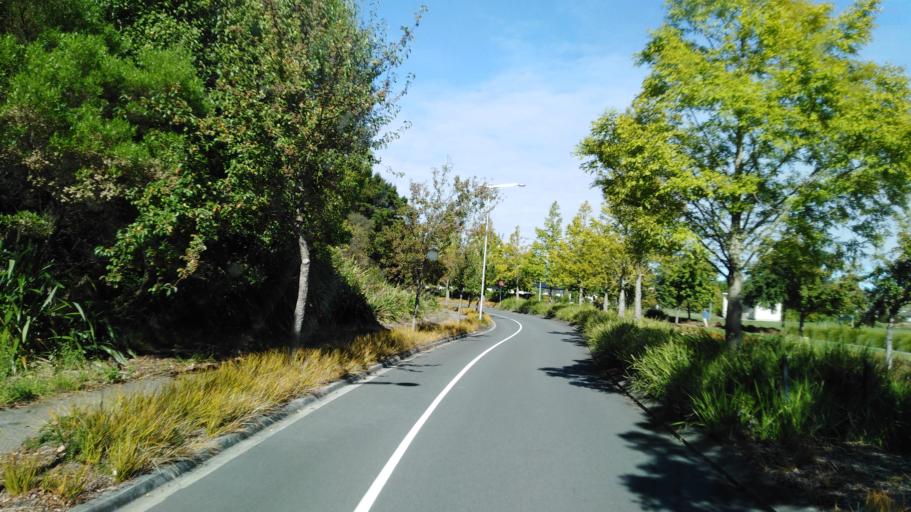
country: NZ
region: Bay of Plenty
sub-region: Tauranga City
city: Tauranga
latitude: -37.7448
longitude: 176.1097
